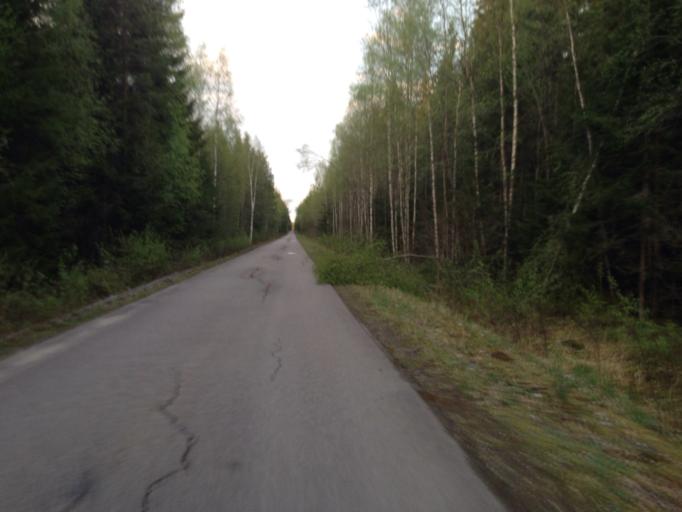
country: SE
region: Dalarna
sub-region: Ludvika Kommun
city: Ludvika
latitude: 60.1411
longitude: 15.1058
